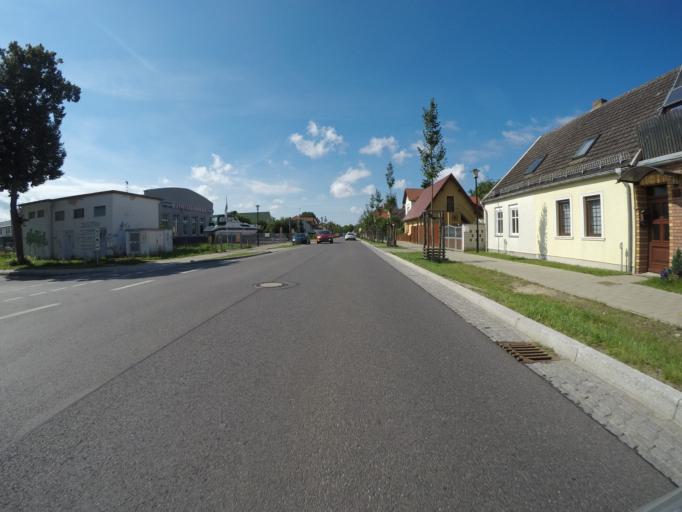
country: DE
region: Brandenburg
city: Rheinsberg
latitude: 53.1048
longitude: 12.8940
